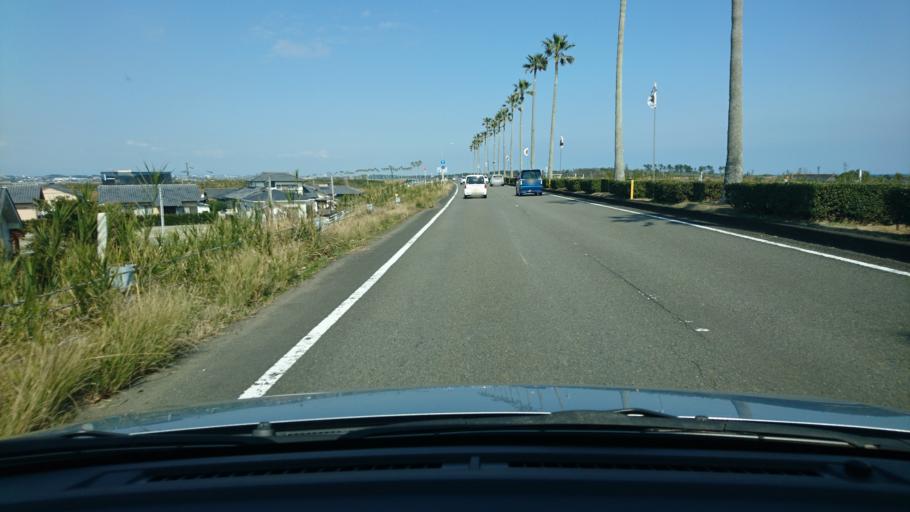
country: JP
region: Miyazaki
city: Miyazaki-shi
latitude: 31.8334
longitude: 131.4441
